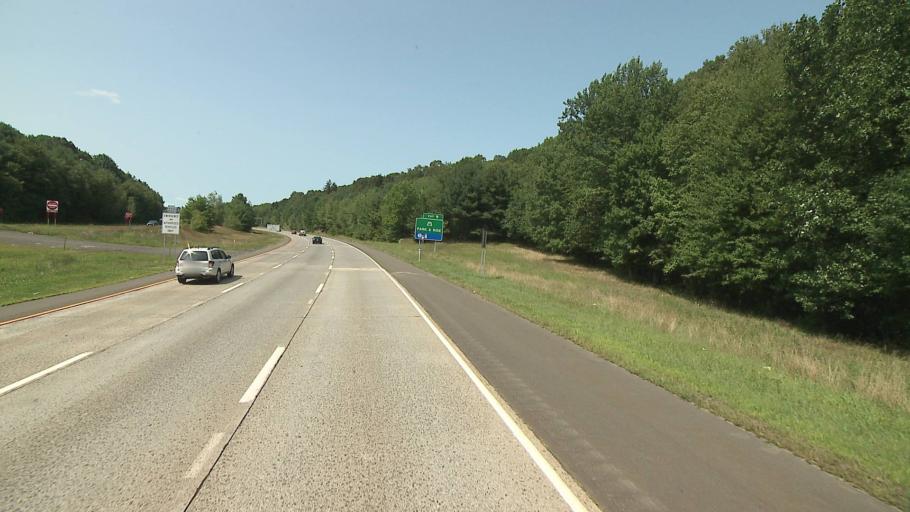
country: US
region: Connecticut
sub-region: Fairfield County
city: Trumbull
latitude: 41.2479
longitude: -73.1905
